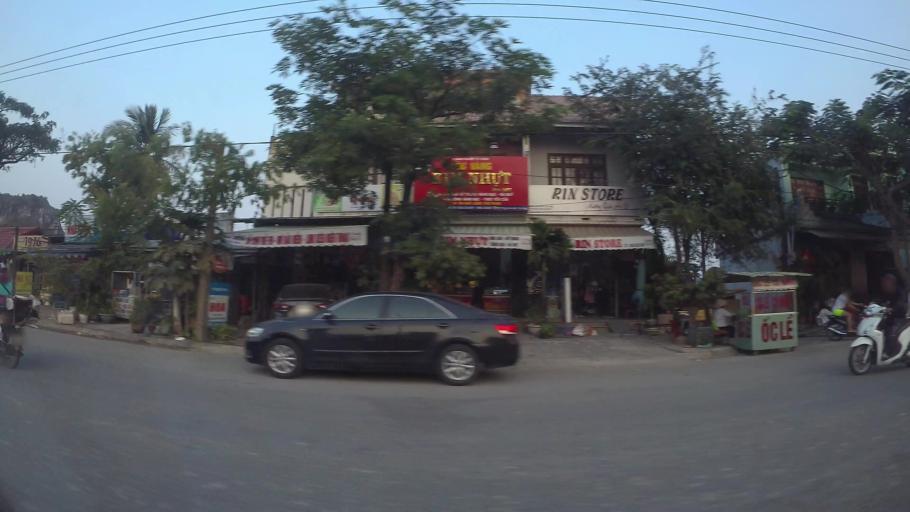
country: VN
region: Da Nang
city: Ngu Hanh Son
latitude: 15.9976
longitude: 108.2594
